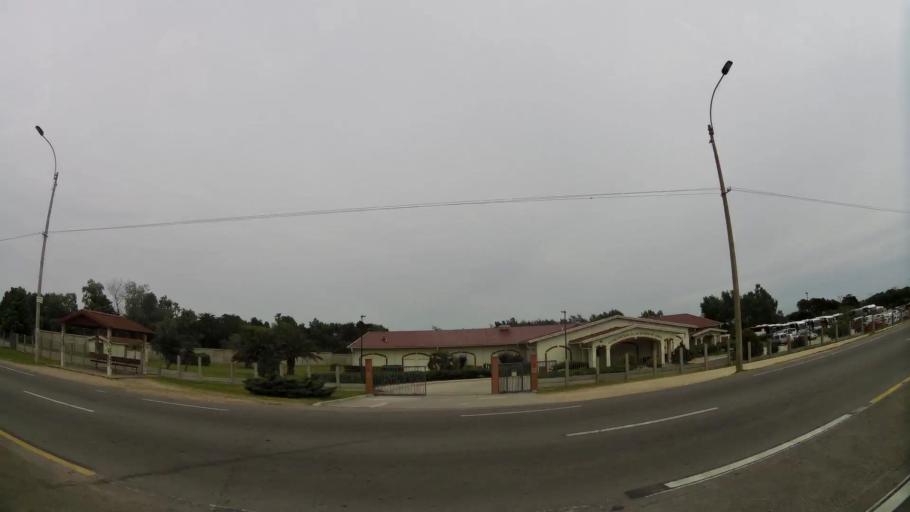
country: UY
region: Canelones
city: La Paz
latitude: -34.7852
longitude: -56.2241
